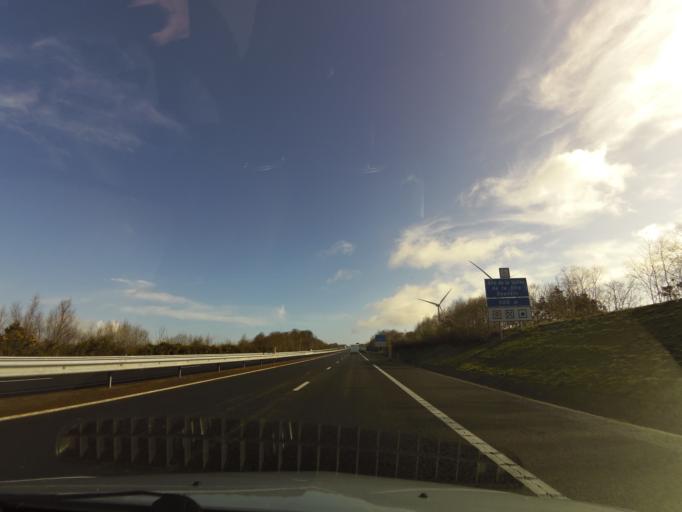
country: FR
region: Lower Normandy
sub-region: Departement de la Manche
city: Percy
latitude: 48.9007
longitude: -1.1132
